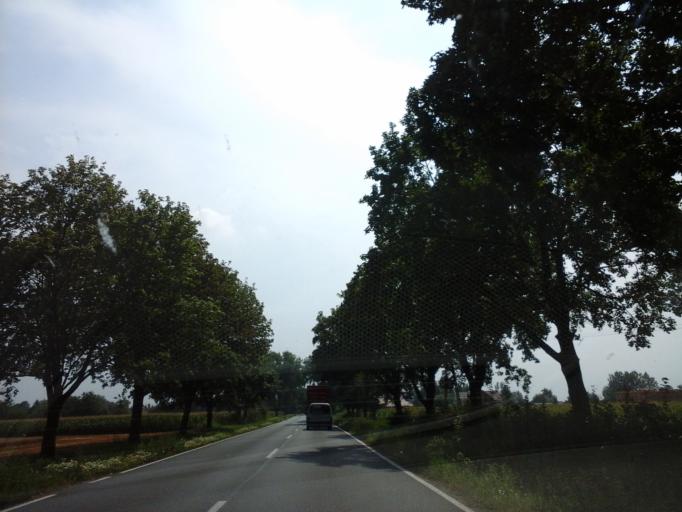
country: PL
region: Lower Silesian Voivodeship
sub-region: Powiat wroclawski
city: Zorawina
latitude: 50.9455
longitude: 17.0702
